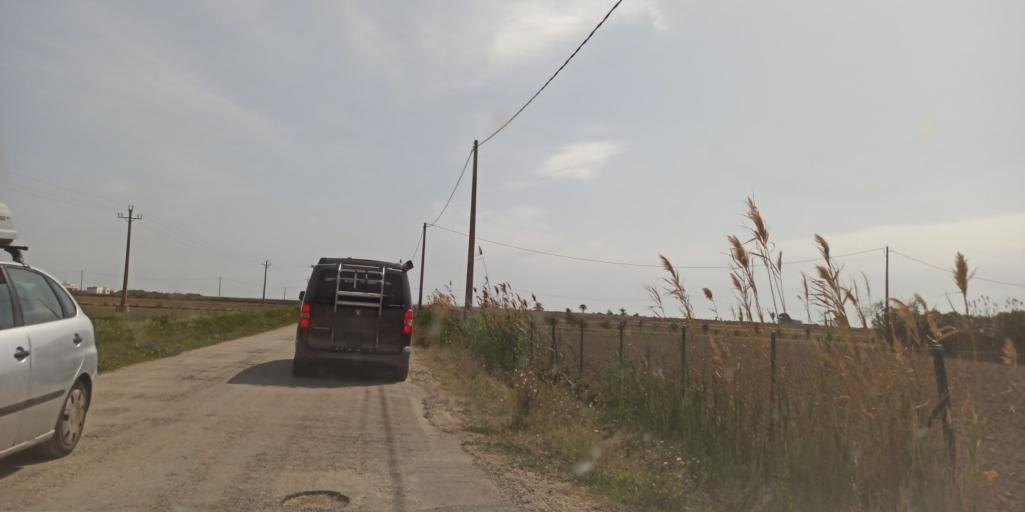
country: ES
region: Catalonia
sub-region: Provincia de Tarragona
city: Deltebre
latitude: 40.6435
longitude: 0.7306
